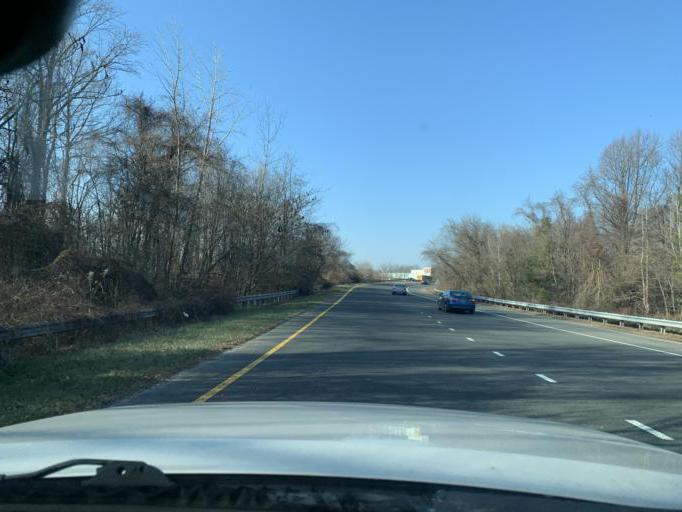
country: US
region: Maryland
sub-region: Prince George's County
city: Largo
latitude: 38.8702
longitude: -76.8422
